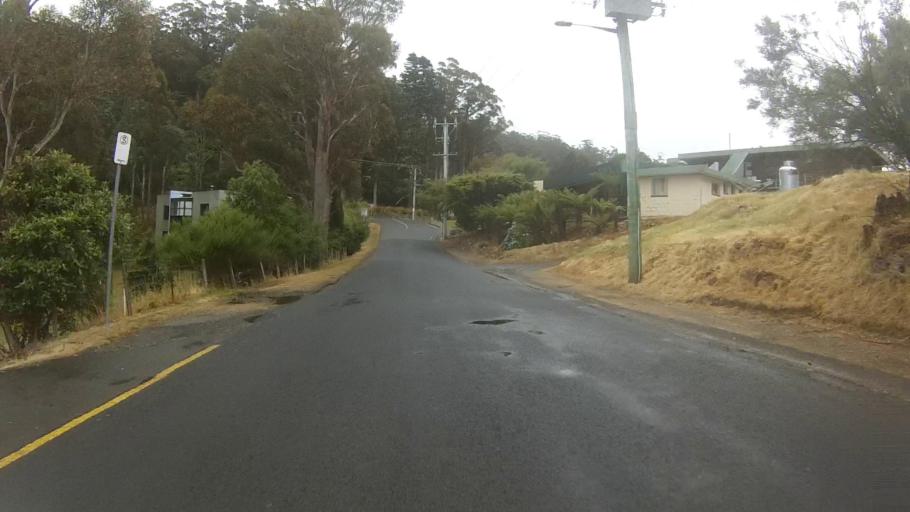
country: AU
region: Tasmania
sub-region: Hobart
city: Dynnyrne
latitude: -42.9230
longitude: 147.2605
